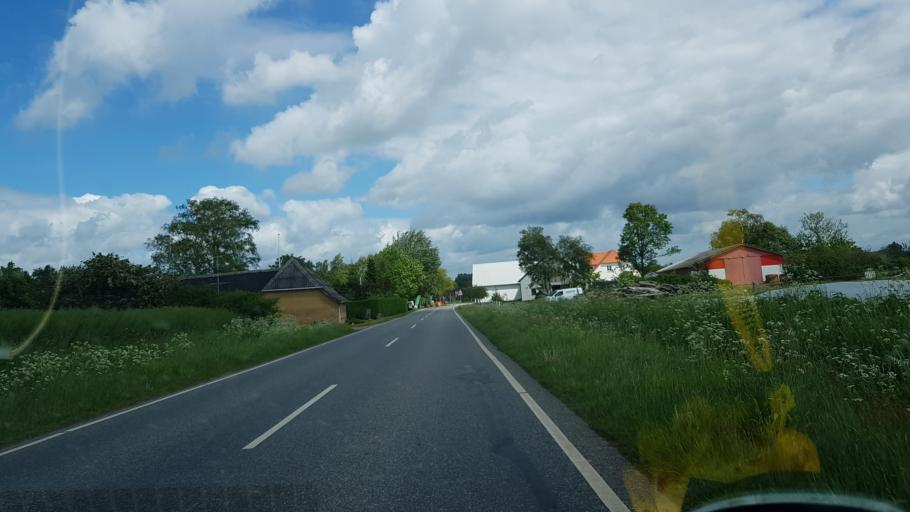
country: DK
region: South Denmark
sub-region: Kolding Kommune
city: Christiansfeld
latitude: 55.3472
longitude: 9.4783
